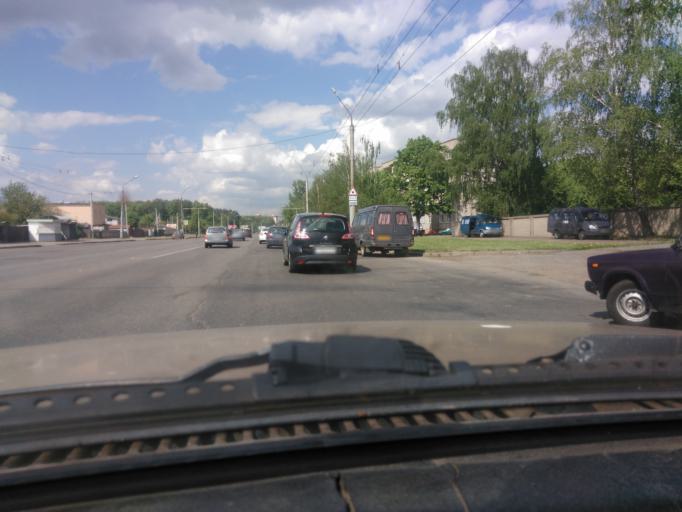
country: BY
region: Mogilev
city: Mahilyow
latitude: 53.9411
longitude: 30.3546
